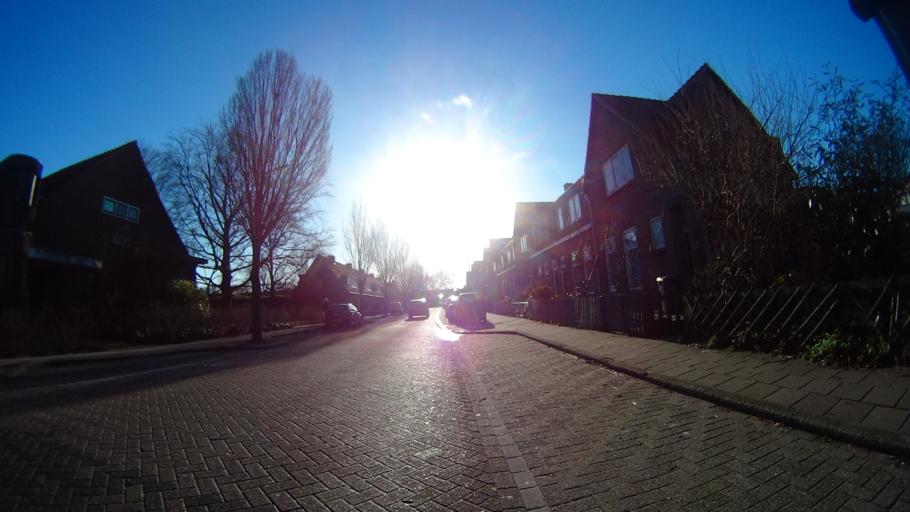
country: NL
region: Utrecht
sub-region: Gemeente Amersfoort
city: Amersfoort
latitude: 52.1614
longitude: 5.3948
